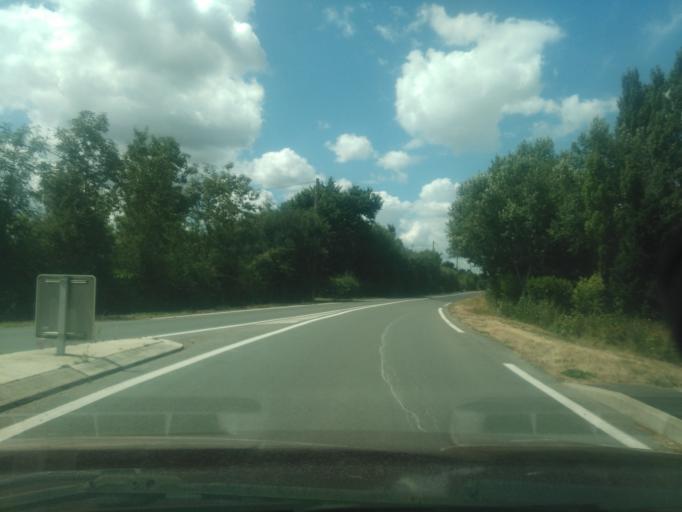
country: FR
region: Pays de la Loire
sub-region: Departement de la Vendee
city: Chauche
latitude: 46.8379
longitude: -1.2840
